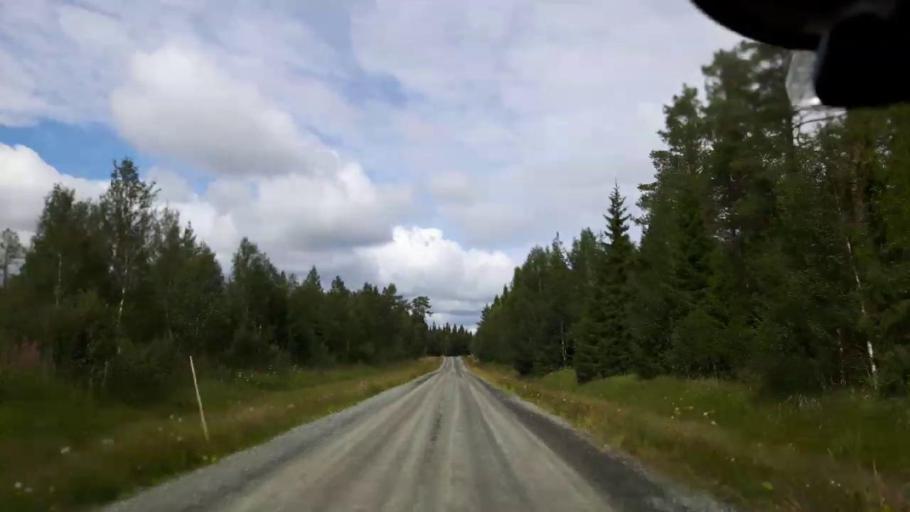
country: SE
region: Jaemtland
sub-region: Krokoms Kommun
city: Valla
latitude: 63.5454
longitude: 13.9169
